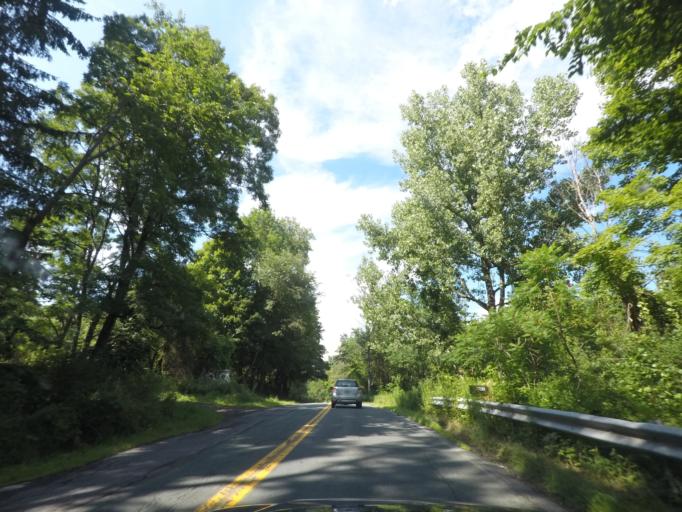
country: US
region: New York
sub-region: Rensselaer County
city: Nassau
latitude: 42.5668
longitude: -73.5689
